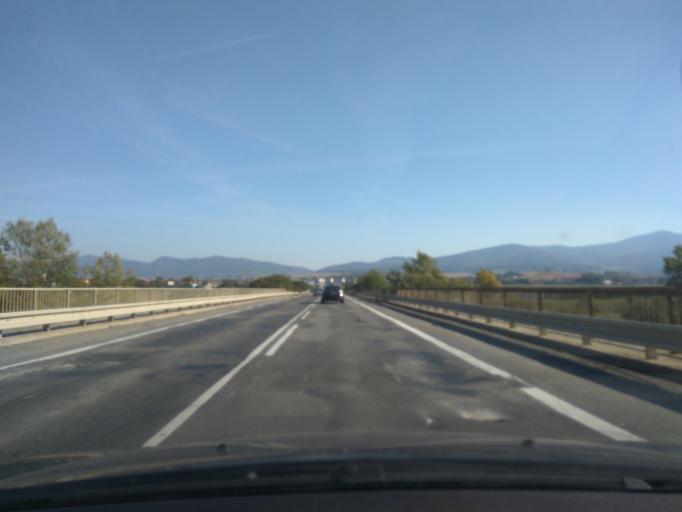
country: SK
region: Trenciansky
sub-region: Okres Trencin
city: Trencin
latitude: 48.8521
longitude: 17.9719
